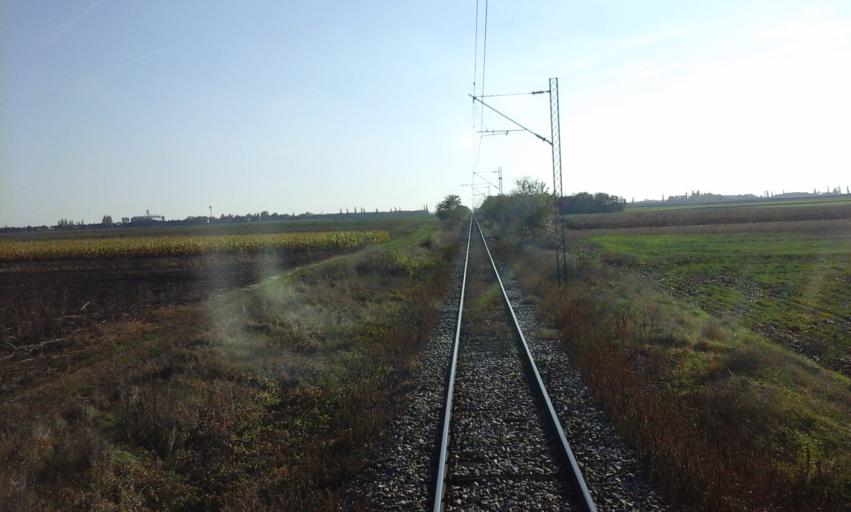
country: RS
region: Autonomna Pokrajina Vojvodina
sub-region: Severnobacki Okrug
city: Backa Topola
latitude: 45.7904
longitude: 19.6475
